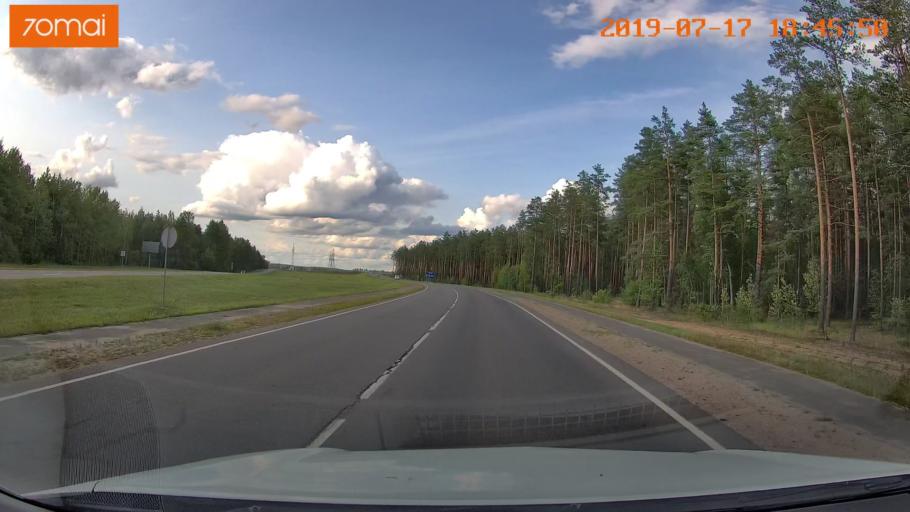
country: BY
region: Mogilev
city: Asipovichy
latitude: 53.3285
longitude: 28.6596
